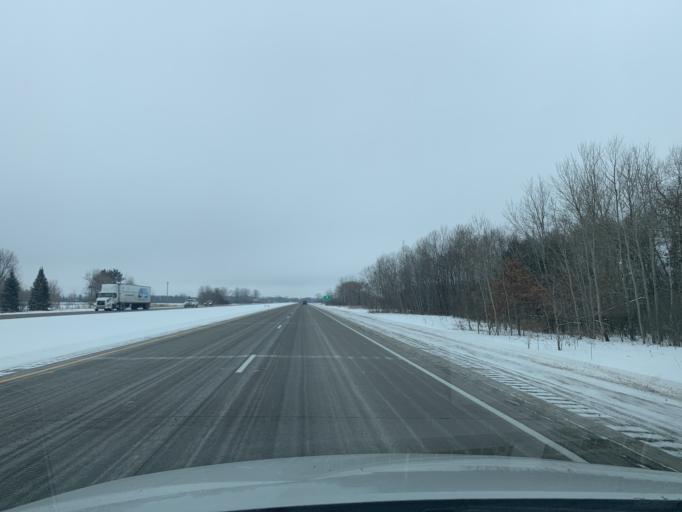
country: US
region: Minnesota
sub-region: Chisago County
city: Rush City
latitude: 45.7044
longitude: -92.9925
